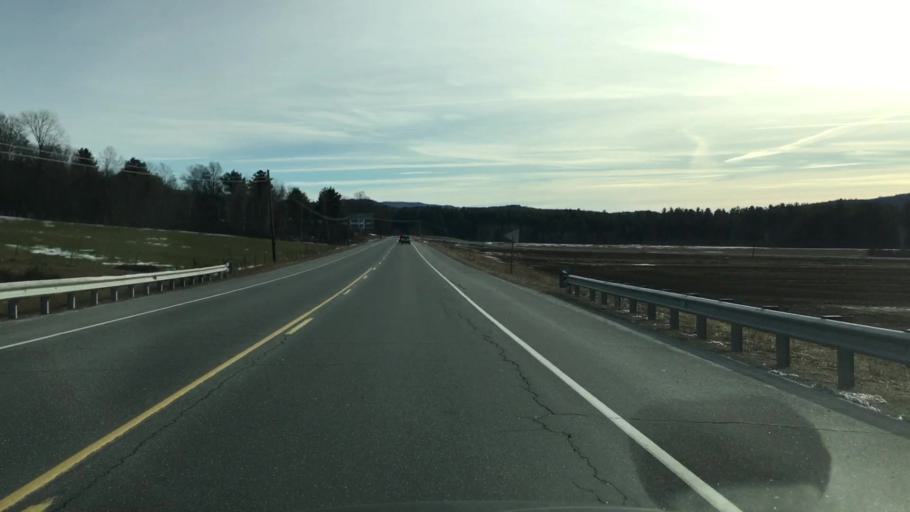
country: US
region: New Hampshire
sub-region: Sullivan County
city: Sunapee
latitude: 43.3673
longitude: -72.1214
